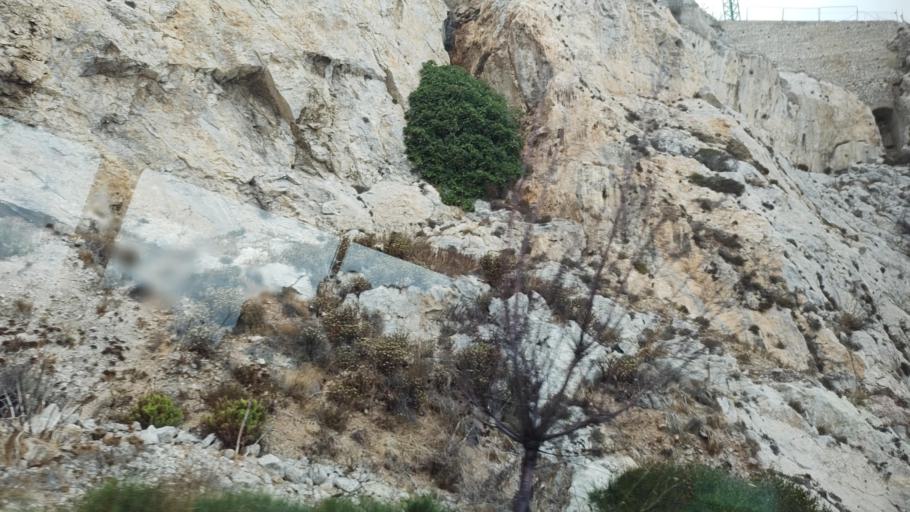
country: GI
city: Gibraltar
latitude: 36.1166
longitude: -5.3494
